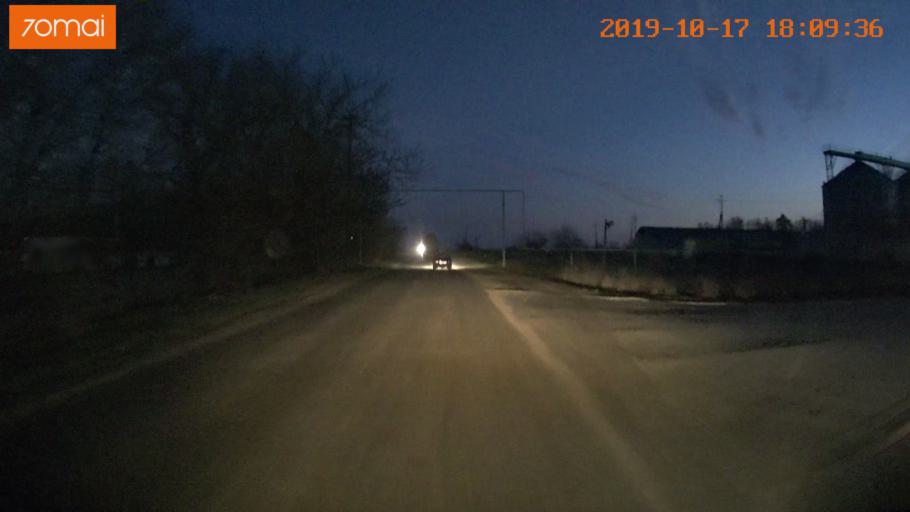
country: RU
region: Tula
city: Kurkino
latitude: 53.4221
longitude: 38.6450
